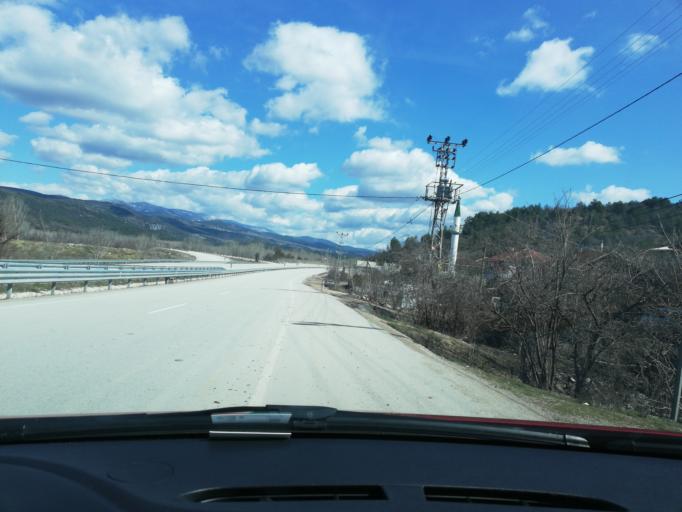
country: TR
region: Kastamonu
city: Igdir
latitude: 41.2301
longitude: 33.0328
